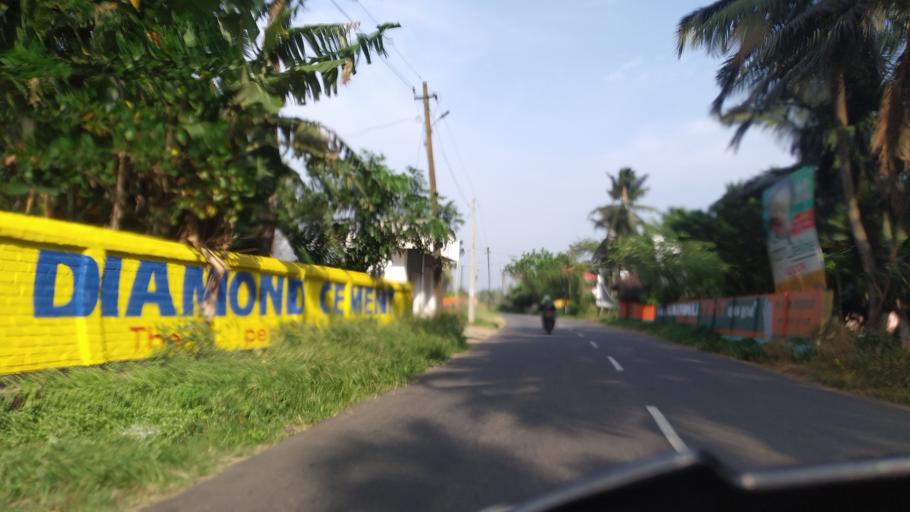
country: IN
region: Kerala
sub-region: Thrissur District
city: Chelakara
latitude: 10.5996
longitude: 76.5344
